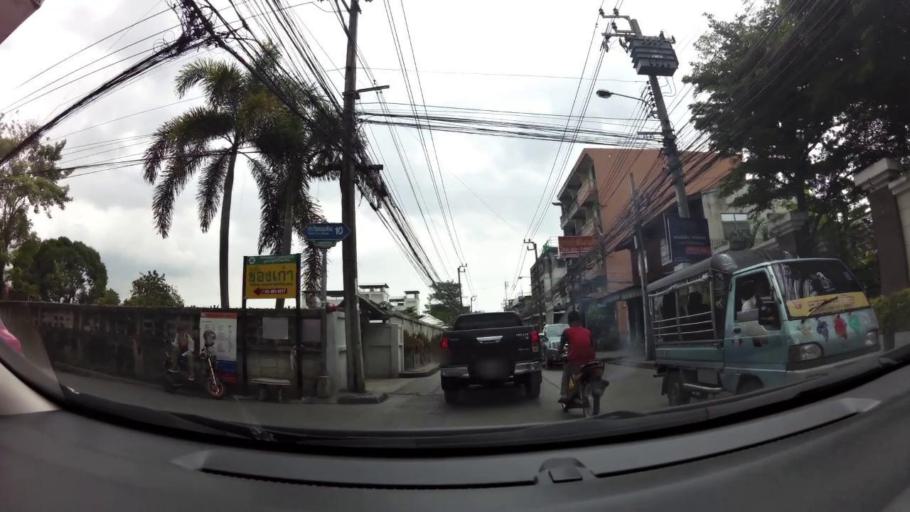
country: TH
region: Bangkok
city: Bang Na
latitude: 13.6841
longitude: 100.6358
